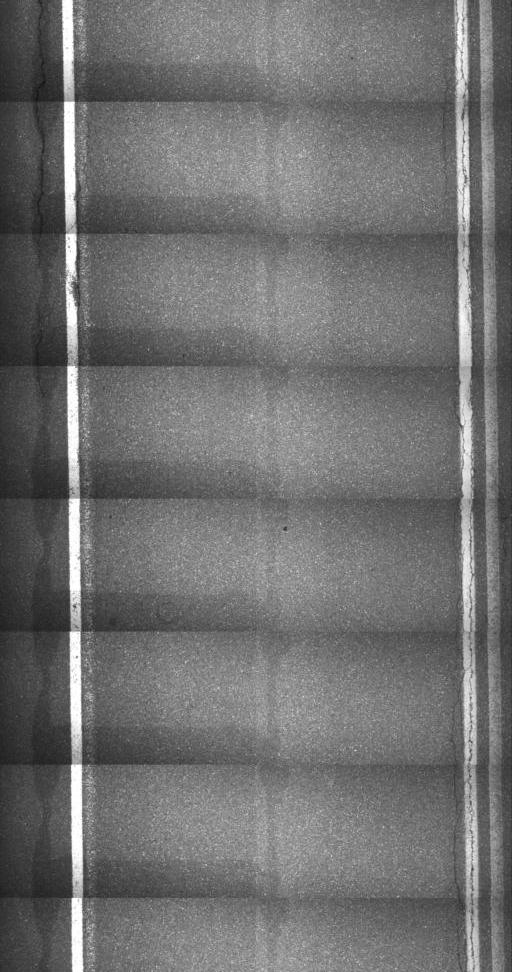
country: CA
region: Quebec
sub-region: Estrie
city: Coaticook
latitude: 45.0010
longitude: -71.7063
